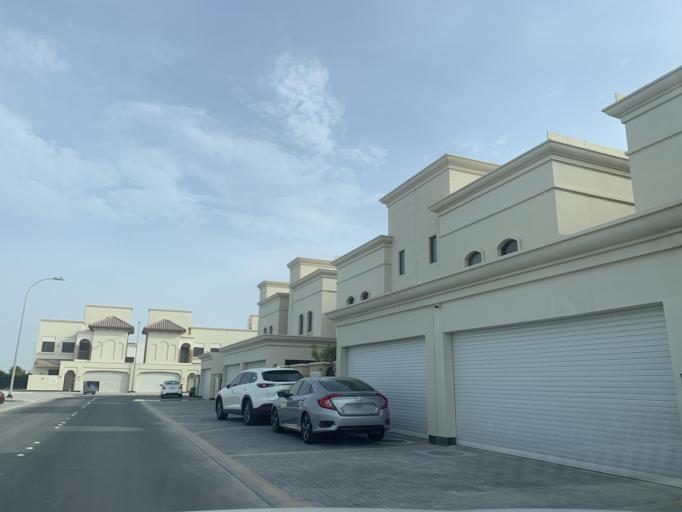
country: BH
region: Muharraq
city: Al Muharraq
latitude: 26.3185
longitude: 50.6304
